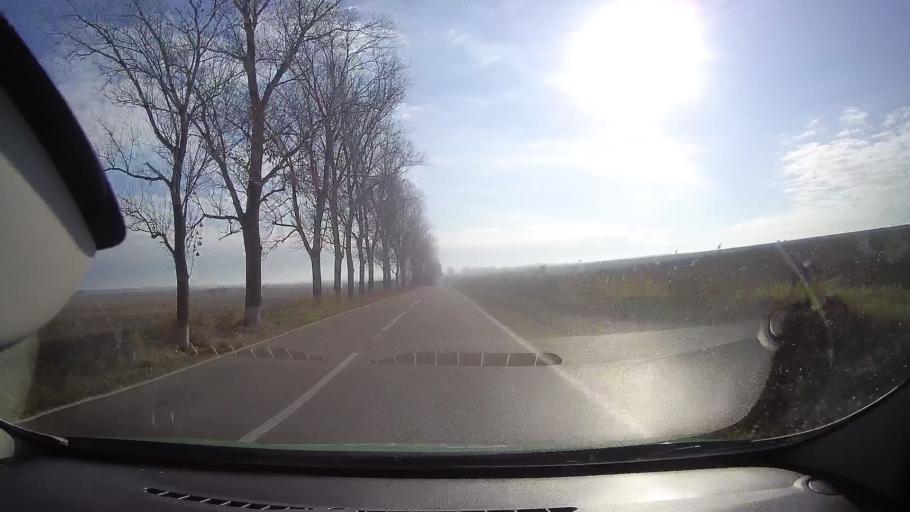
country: RO
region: Tulcea
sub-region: Comuna Mahmudia
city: Mahmudia
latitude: 45.0658
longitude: 29.1073
